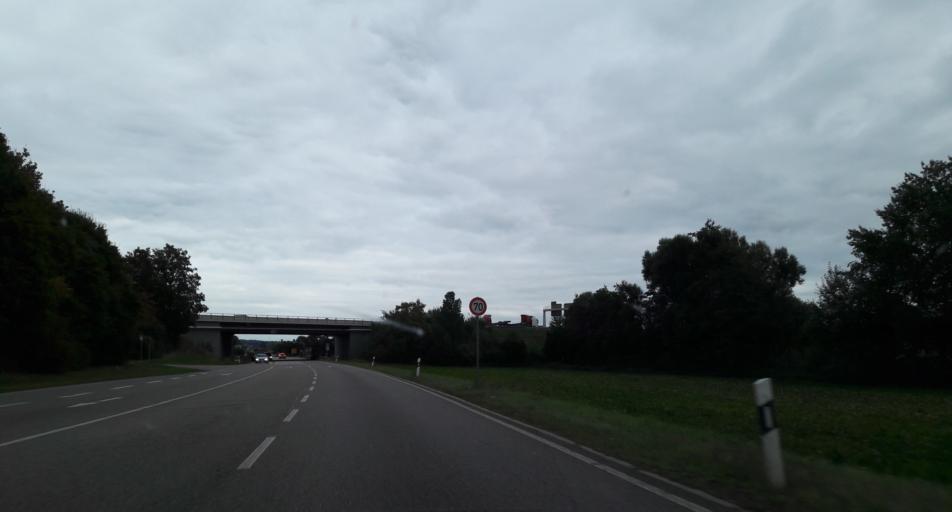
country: DE
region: Baden-Wuerttemberg
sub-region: Regierungsbezirk Stuttgart
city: Bad Rappenau
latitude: 49.2100
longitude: 9.0722
